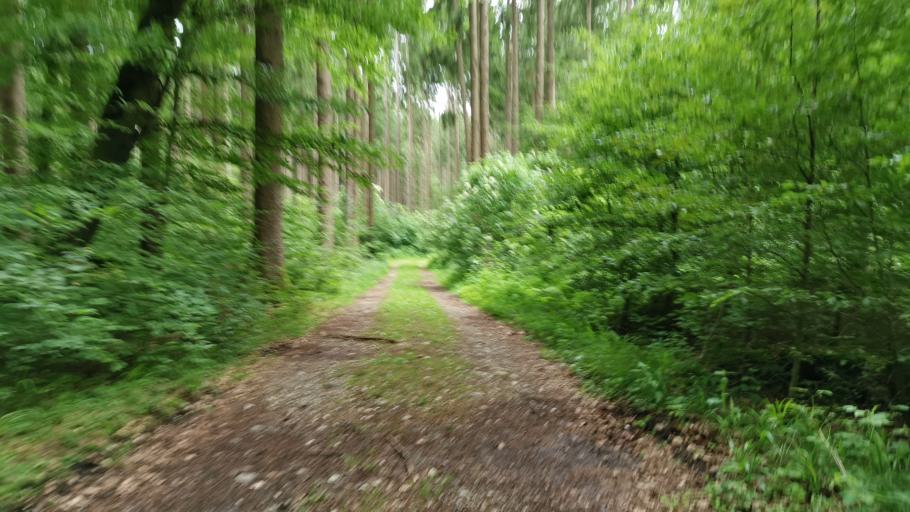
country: DE
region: Bavaria
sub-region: Upper Bavaria
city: Schaftlarn
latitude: 48.0039
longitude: 11.4416
